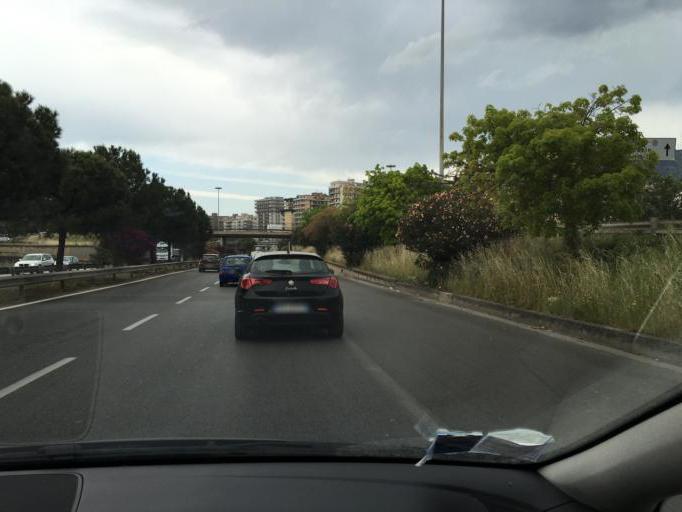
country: IT
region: Sicily
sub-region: Palermo
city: Palermo
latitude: 38.1380
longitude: 13.3311
